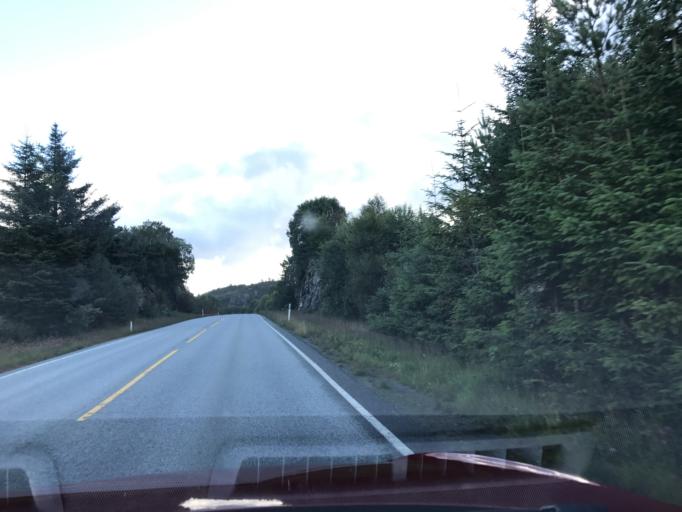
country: NO
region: Hordaland
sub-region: Sveio
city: Sveio
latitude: 59.4930
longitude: 5.3253
